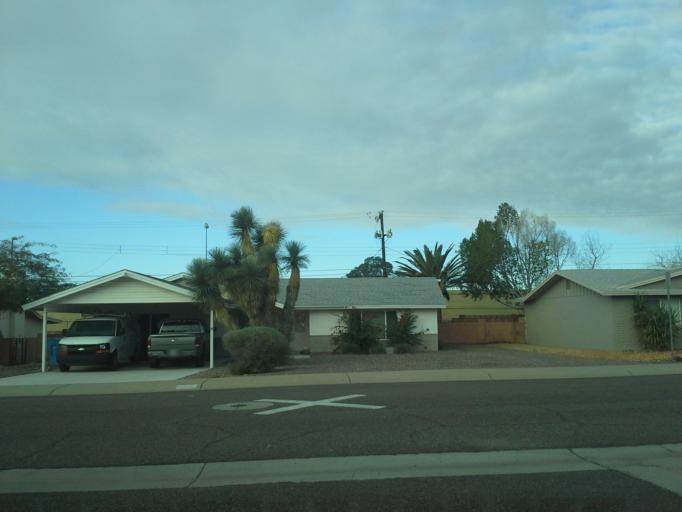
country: US
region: Arizona
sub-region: Maricopa County
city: Phoenix
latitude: 33.5360
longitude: -112.0405
